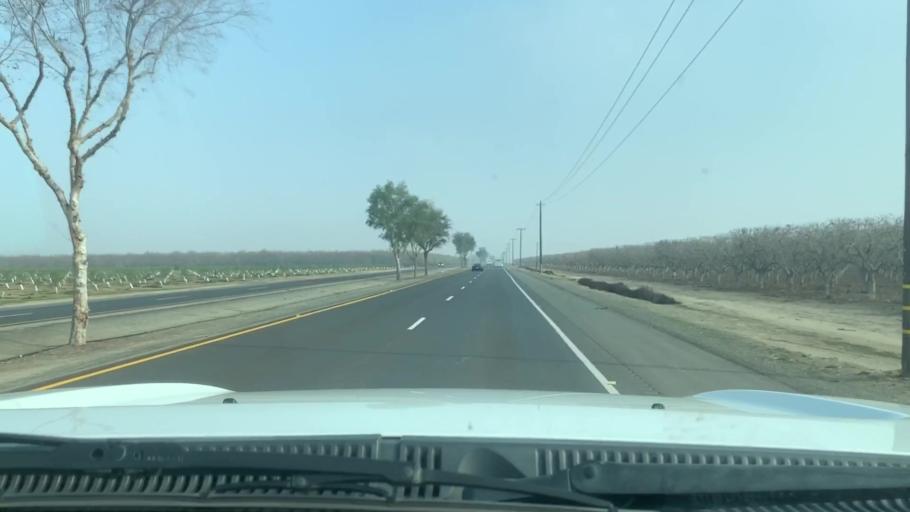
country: US
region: California
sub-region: Kern County
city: Shafter
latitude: 35.4997
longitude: -119.2177
